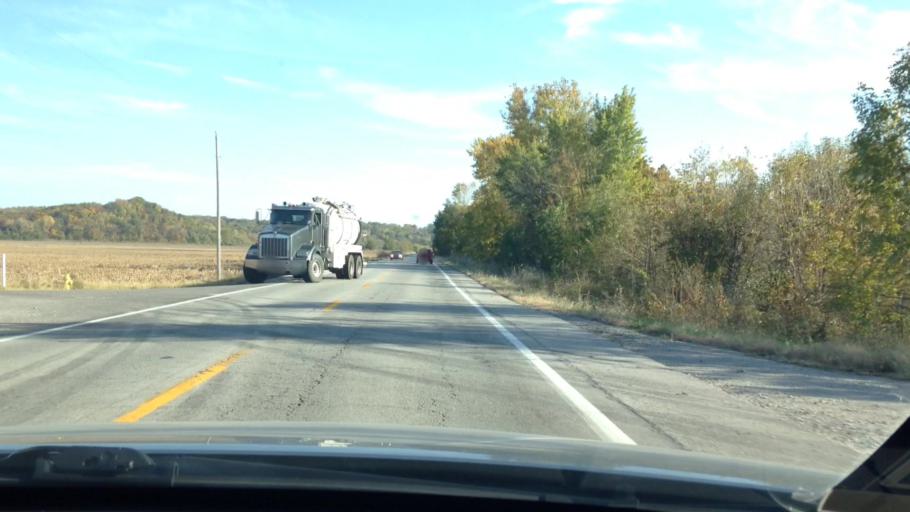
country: US
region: Kansas
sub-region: Leavenworth County
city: Lansing
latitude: 39.2670
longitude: -94.8191
